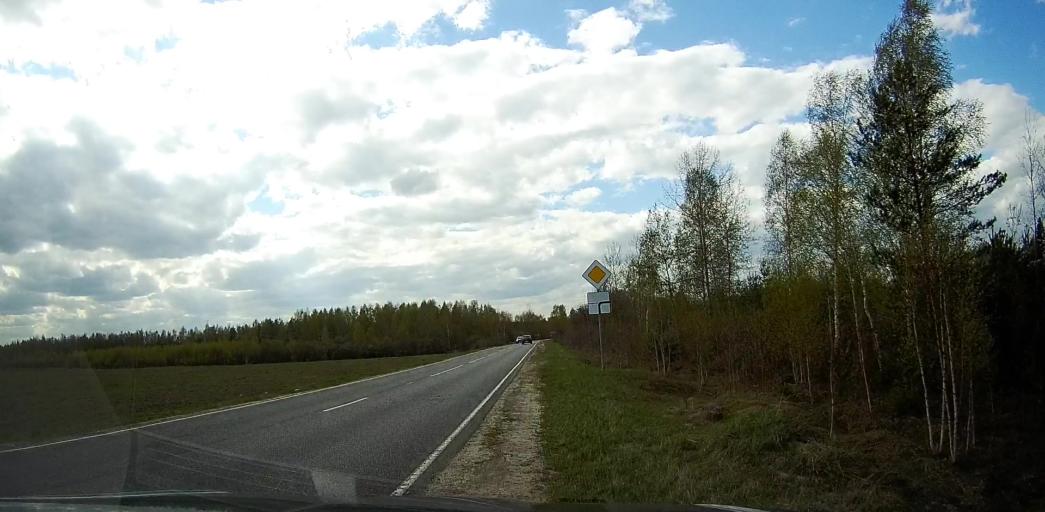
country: RU
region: Moskovskaya
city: Rakhmanovo
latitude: 55.6527
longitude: 38.6428
